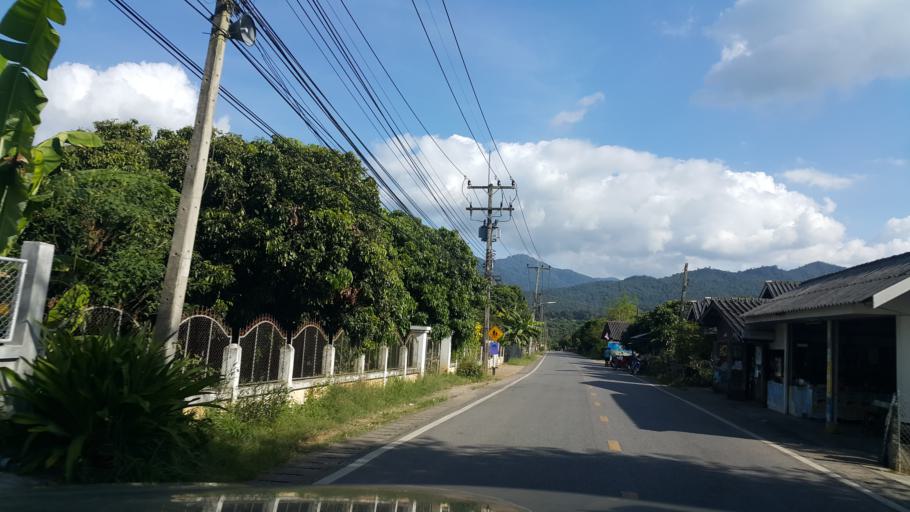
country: TH
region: Lamphun
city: Mae Tha
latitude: 18.5287
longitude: 99.2305
